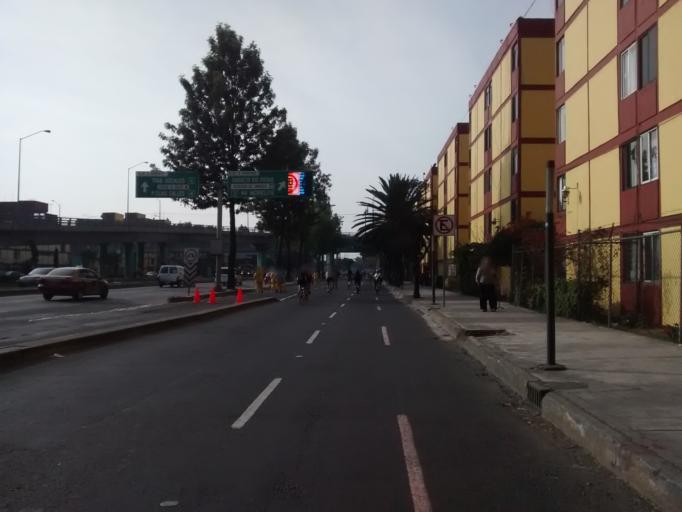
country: MX
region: Mexico City
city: Mexico City
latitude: 19.4150
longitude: -99.1128
